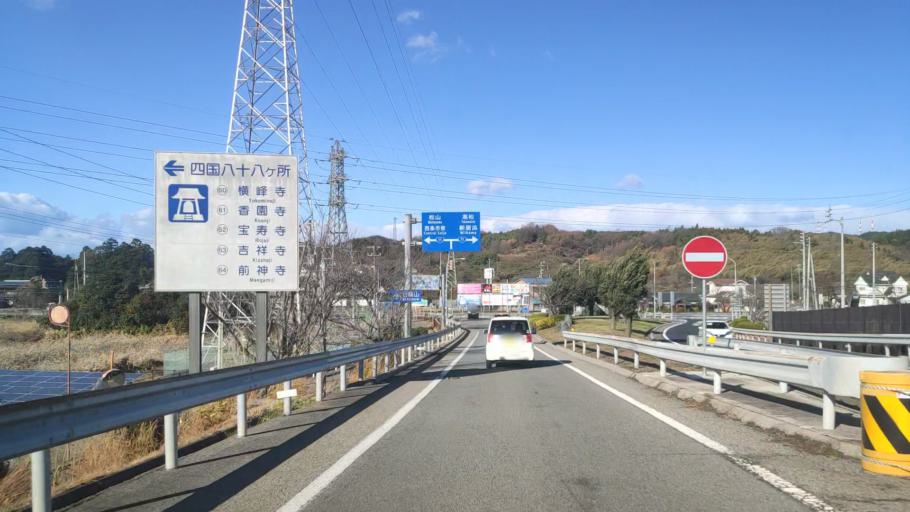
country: JP
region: Ehime
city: Saijo
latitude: 33.9184
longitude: 133.2404
